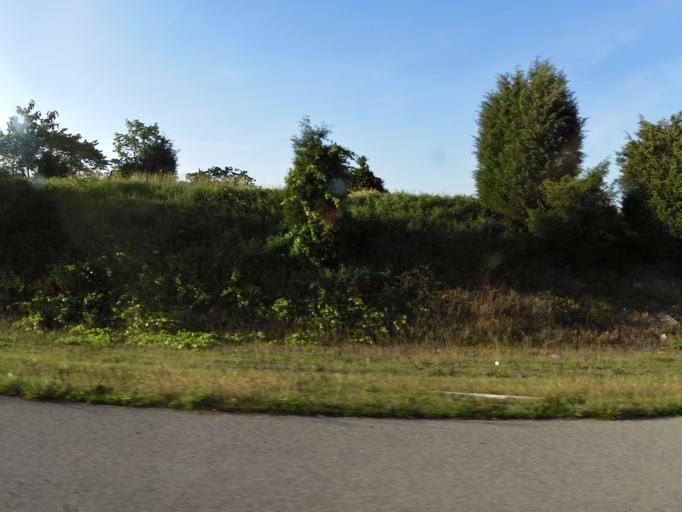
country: US
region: Tennessee
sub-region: Blount County
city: Louisville
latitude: 35.8587
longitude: -84.0700
